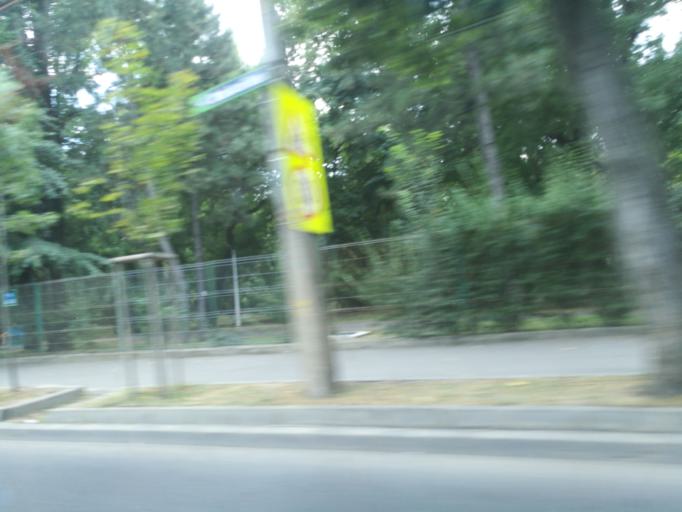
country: RO
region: Ilfov
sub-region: Comuna Chiajna
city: Rosu
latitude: 44.4888
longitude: 26.0361
